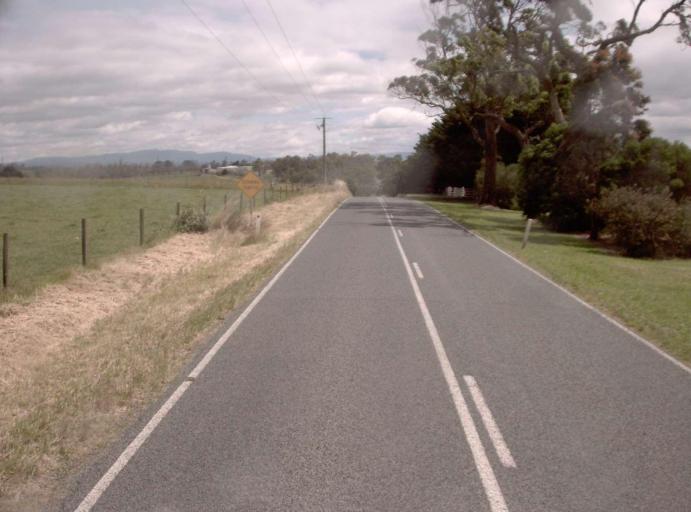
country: AU
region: Victoria
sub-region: Latrobe
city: Moe
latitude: -38.1599
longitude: 146.1437
